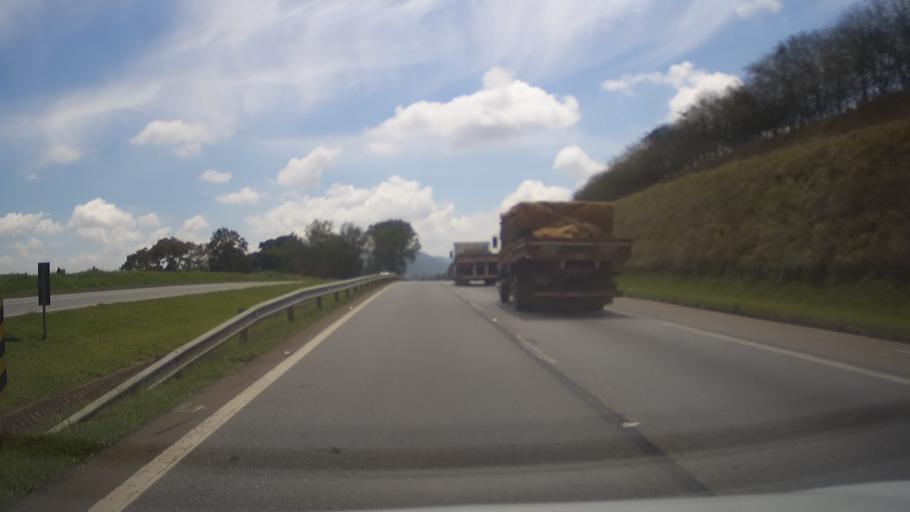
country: BR
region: Minas Gerais
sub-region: Santa Rita Do Sapucai
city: Santa Rita do Sapucai
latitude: -22.1003
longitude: -45.7208
